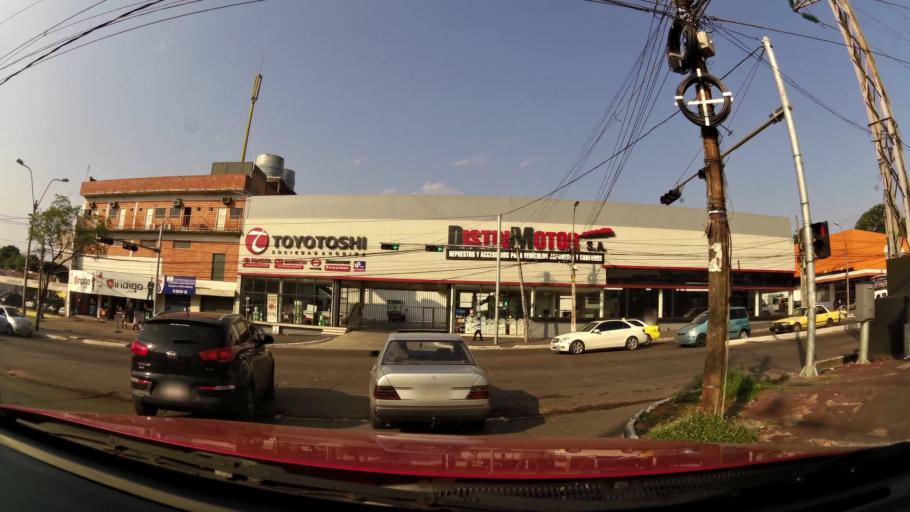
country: PY
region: Central
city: Lambare
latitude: -25.3374
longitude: -57.5867
